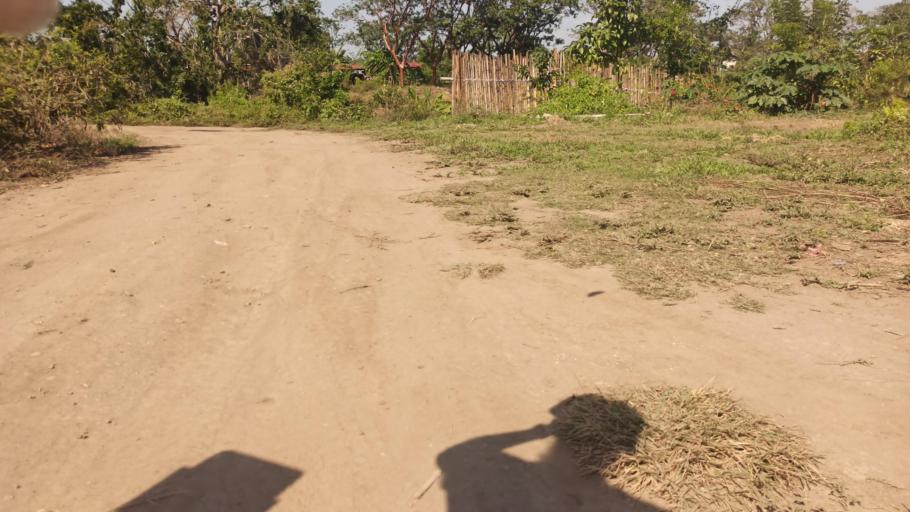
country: MX
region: Puebla
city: San Jose Acateno
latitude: 20.1628
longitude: -97.1651
